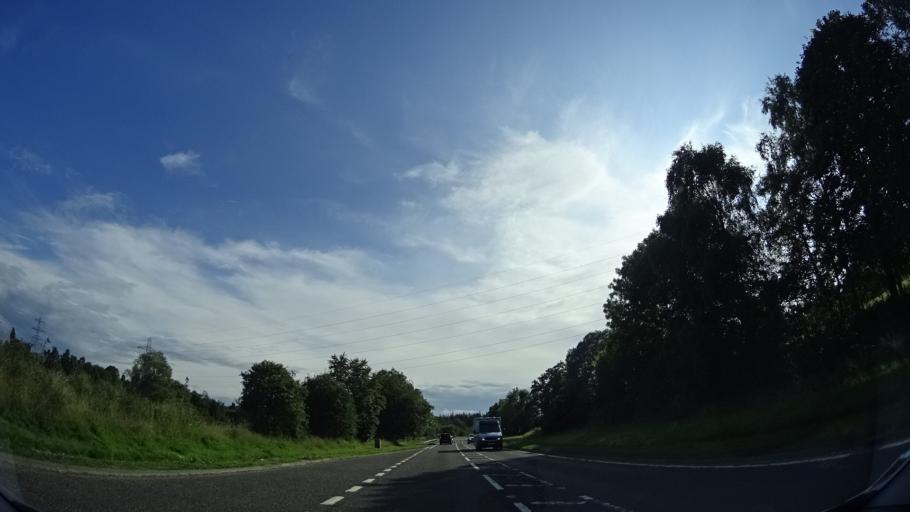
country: GB
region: Scotland
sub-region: Highland
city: Conon Bridge
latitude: 57.5759
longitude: -4.4489
